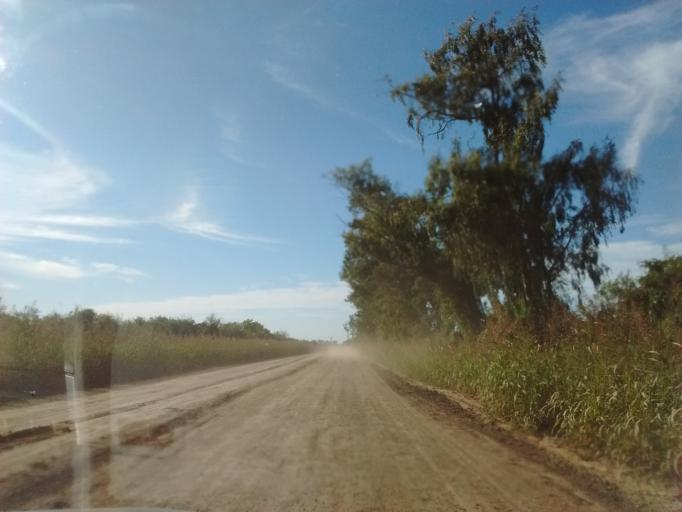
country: AR
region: Santa Fe
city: Coronda
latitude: -32.2303
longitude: -60.9685
